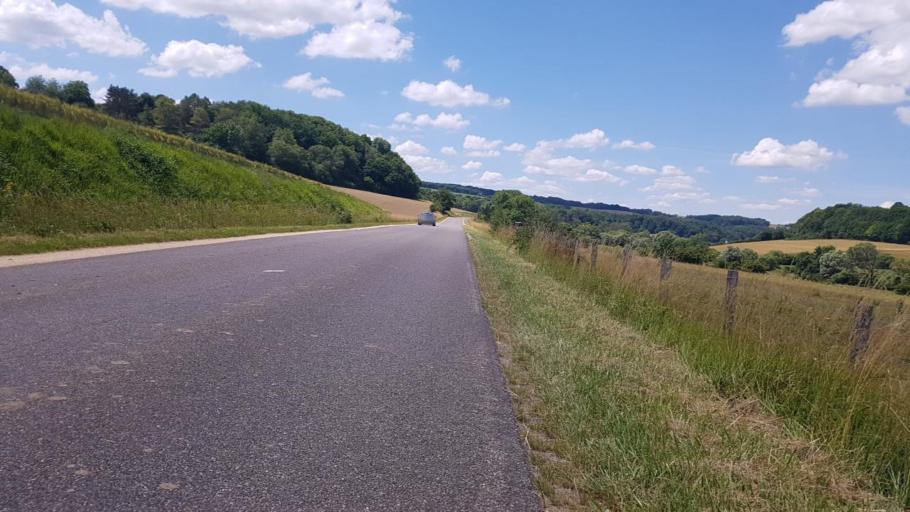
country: FR
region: Lorraine
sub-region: Departement de la Meuse
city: Vacon
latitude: 48.6324
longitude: 5.4869
